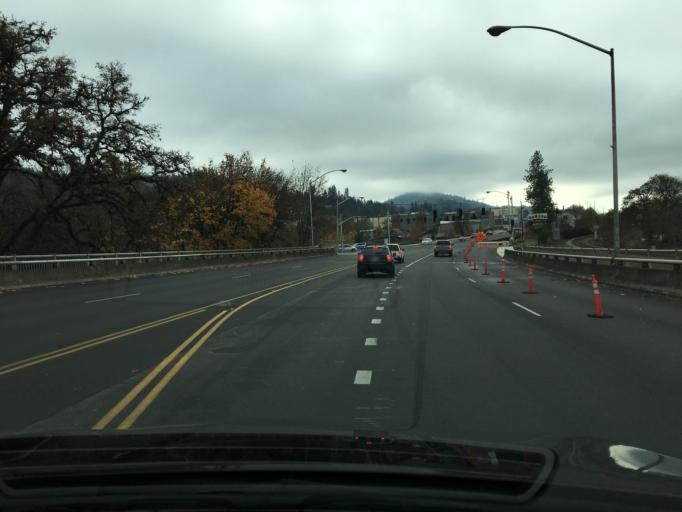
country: US
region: Oregon
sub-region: Douglas County
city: Roseburg
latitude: 43.2147
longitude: -123.3427
